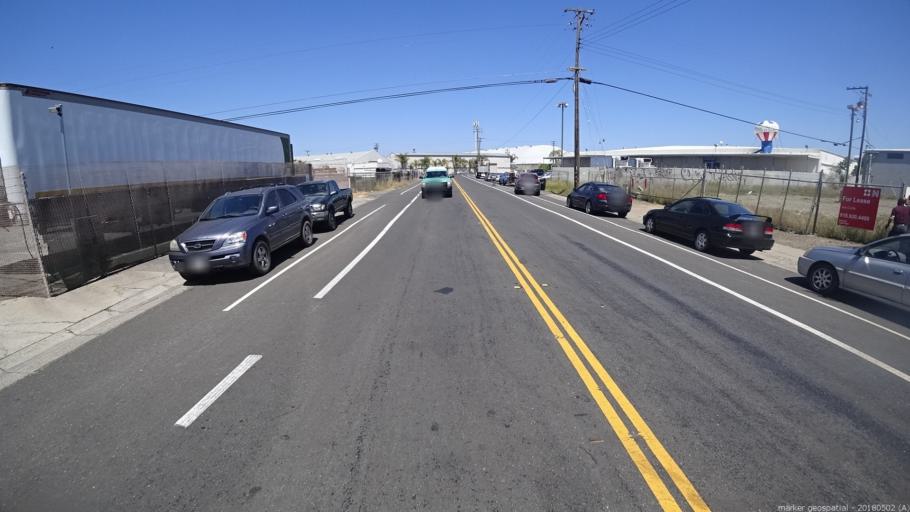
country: US
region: California
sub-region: Sacramento County
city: Sacramento
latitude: 38.6011
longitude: -121.4401
